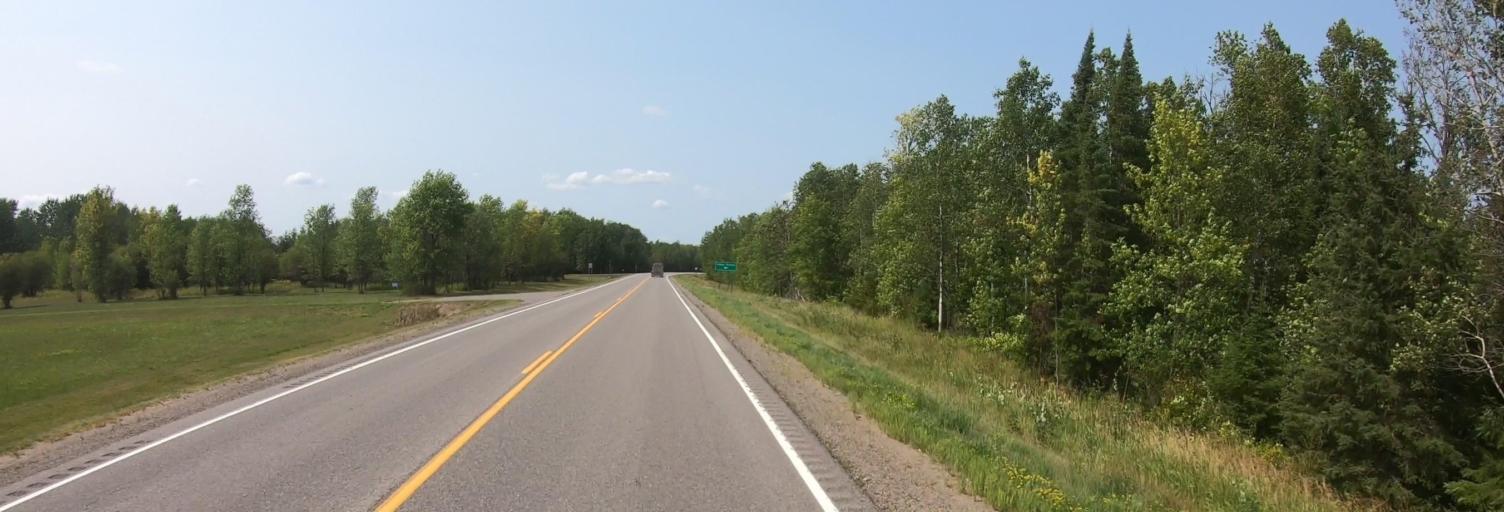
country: US
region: Minnesota
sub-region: Koochiching County
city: International Falls
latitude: 48.6307
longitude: -93.8947
